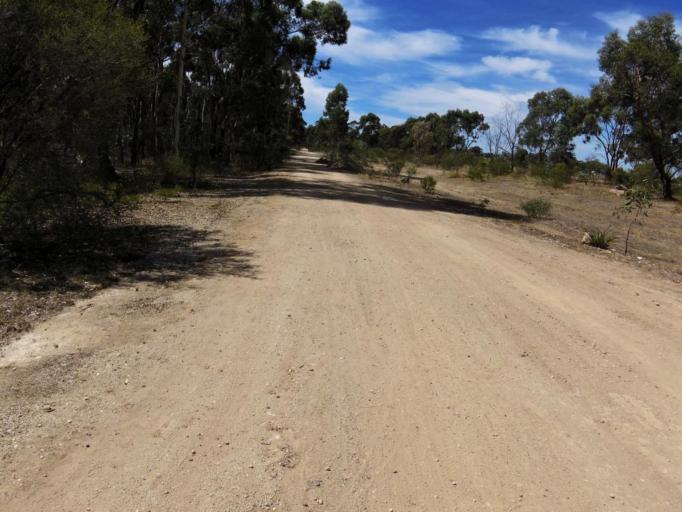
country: AU
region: Victoria
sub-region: Greater Bendigo
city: White Hills
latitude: -36.7541
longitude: 144.3253
